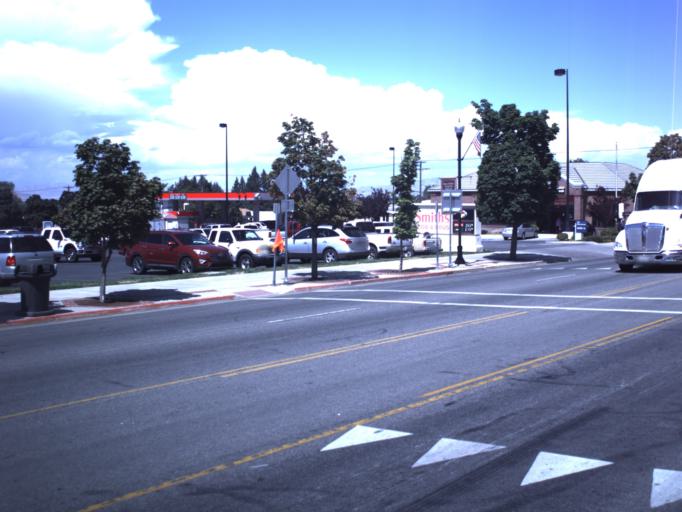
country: US
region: Utah
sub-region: Box Elder County
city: Brigham City
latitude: 41.5070
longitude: -112.0158
